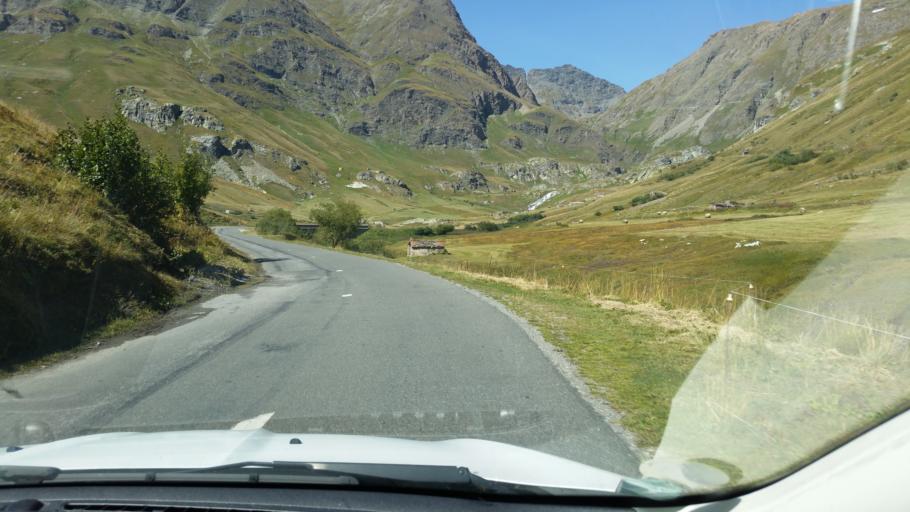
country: FR
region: Rhone-Alpes
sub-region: Departement de la Savoie
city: Val-d'Isere
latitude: 45.3833
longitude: 7.0448
